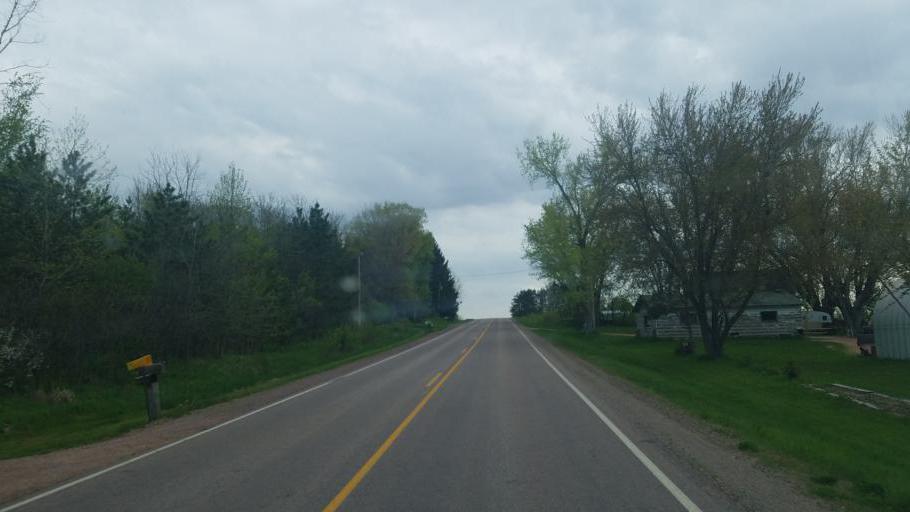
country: US
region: Wisconsin
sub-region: Wood County
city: Marshfield
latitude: 44.5899
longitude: -90.2990
